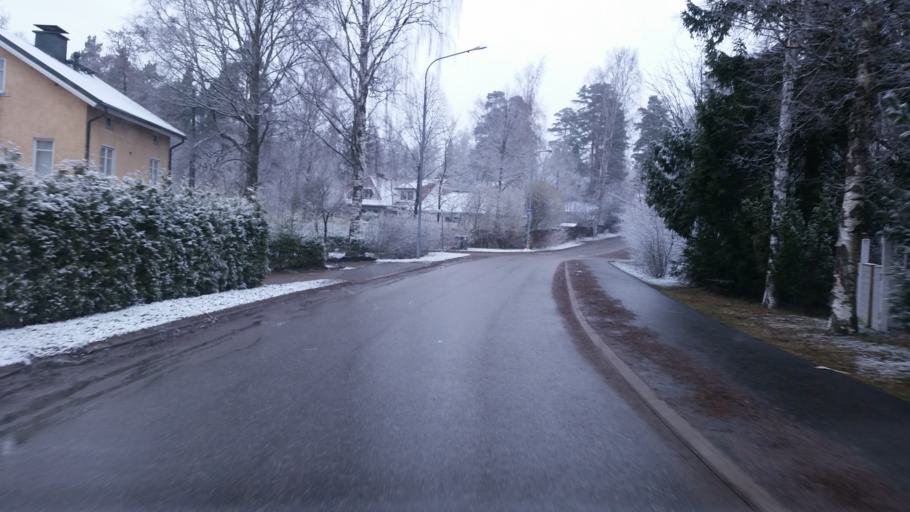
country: FI
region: Uusimaa
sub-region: Helsinki
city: Koukkuniemi
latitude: 60.1631
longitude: 24.7604
